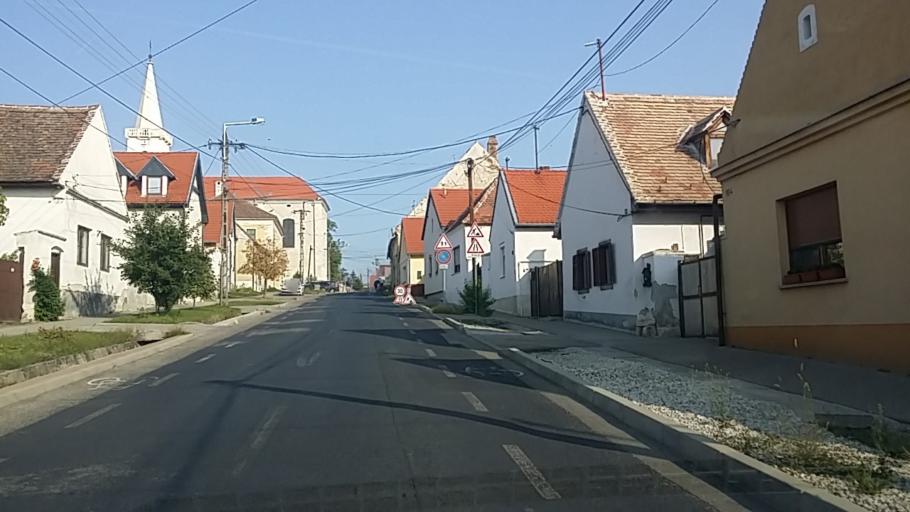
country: HU
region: Gyor-Moson-Sopron
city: Fertorakos
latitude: 47.7181
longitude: 16.6526
